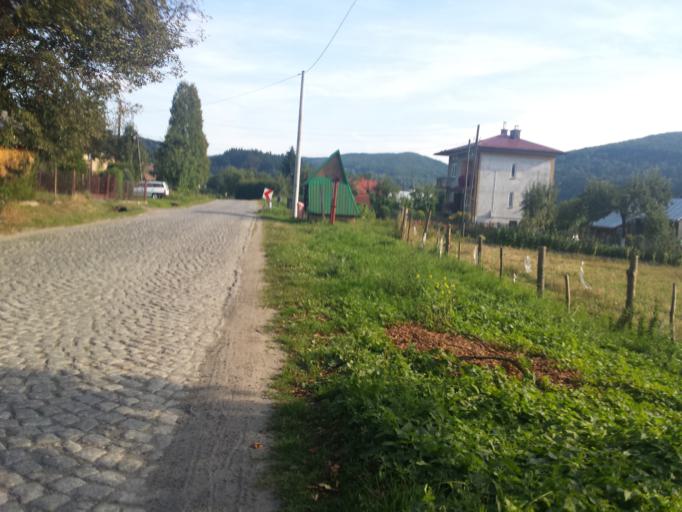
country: PL
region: Subcarpathian Voivodeship
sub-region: Powiat leski
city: Uherce Mineralne
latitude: 49.4411
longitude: 22.4089
